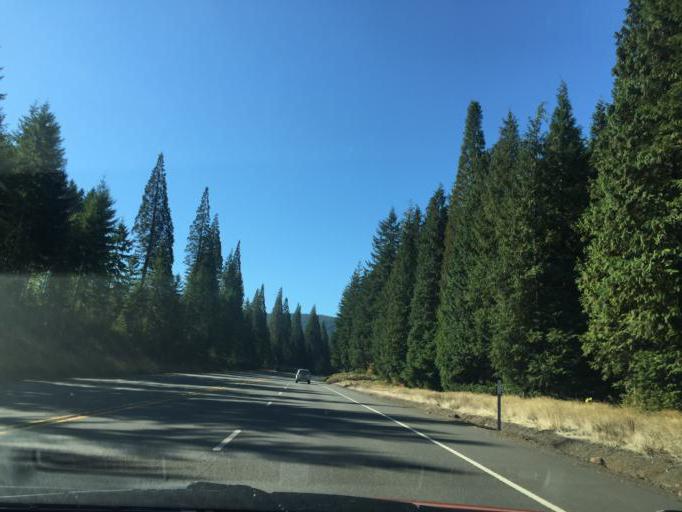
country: US
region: Oregon
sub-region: Columbia County
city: Vernonia
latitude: 45.7765
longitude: -123.3645
